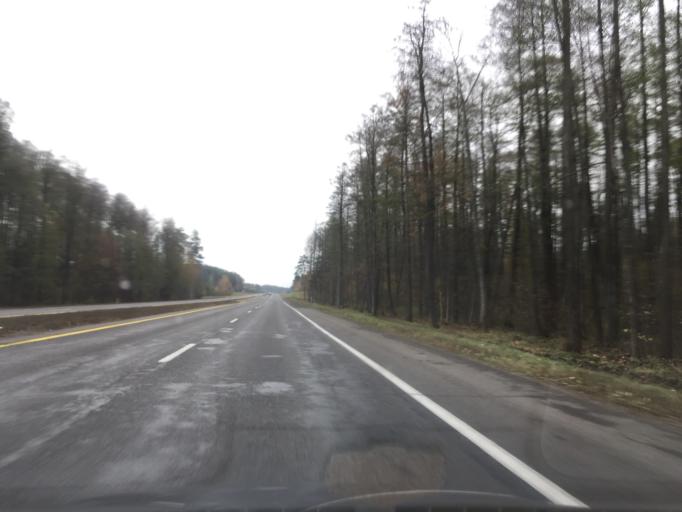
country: BY
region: Gomel
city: Horad Rechytsa
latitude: 52.3549
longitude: 30.6135
